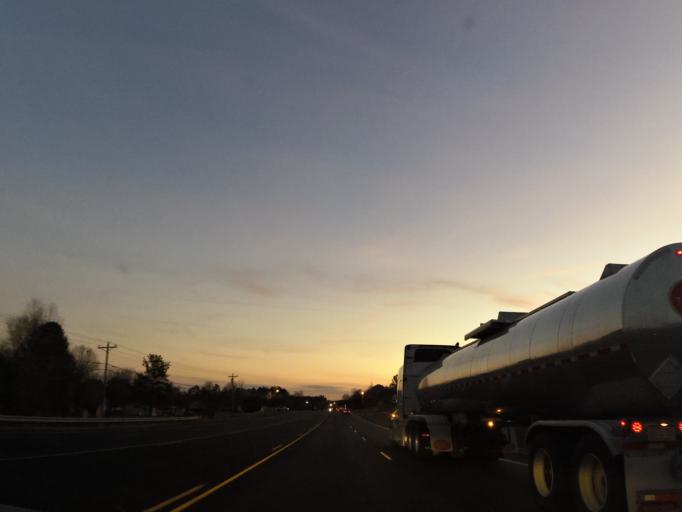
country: US
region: Georgia
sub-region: Whitfield County
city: Varnell
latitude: 34.9133
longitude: -84.9460
